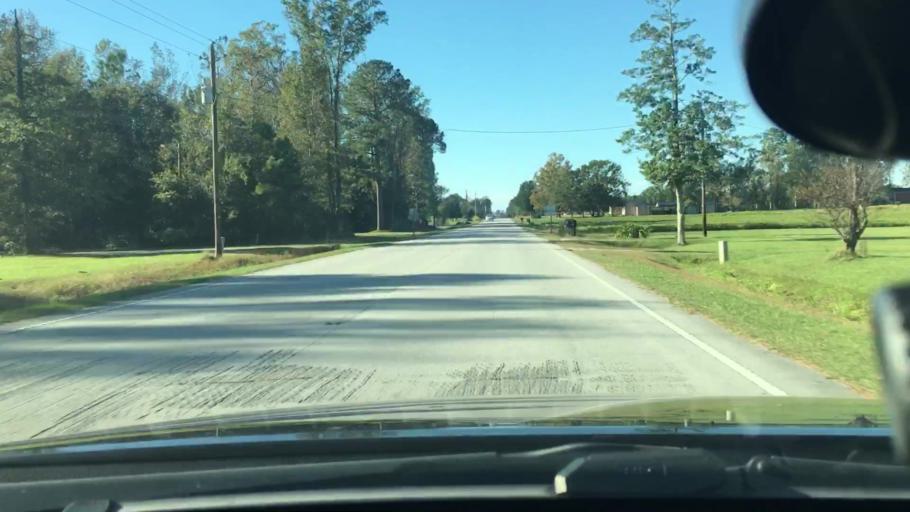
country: US
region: North Carolina
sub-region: Craven County
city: Vanceboro
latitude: 35.3609
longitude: -77.1976
